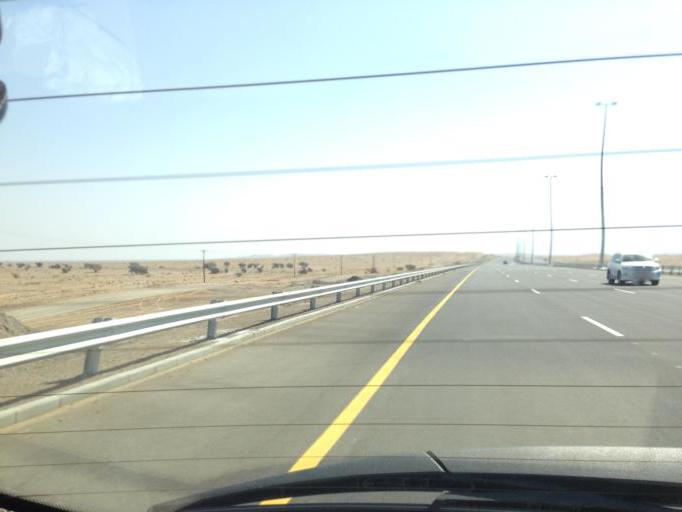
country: OM
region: Al Batinah
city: Rustaq
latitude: 23.5323
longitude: 57.5812
